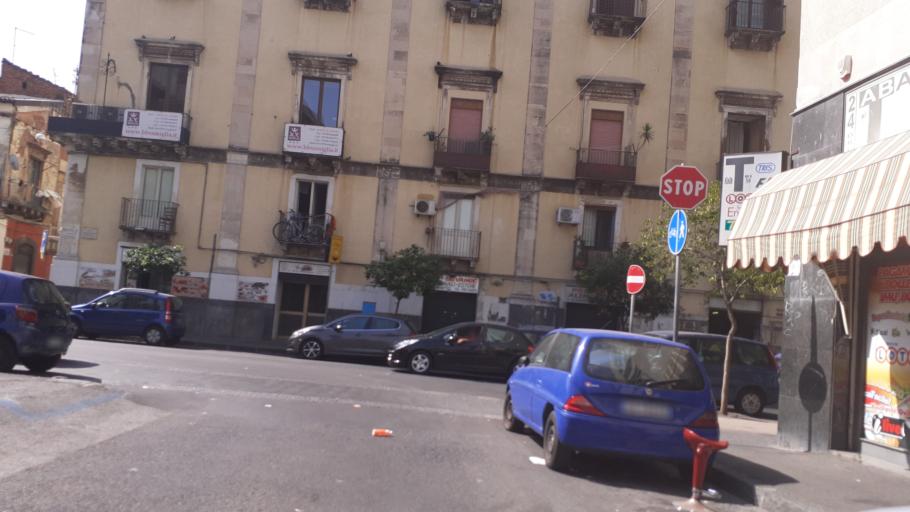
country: IT
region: Sicily
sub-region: Catania
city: Catania
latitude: 37.5067
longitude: 15.0929
